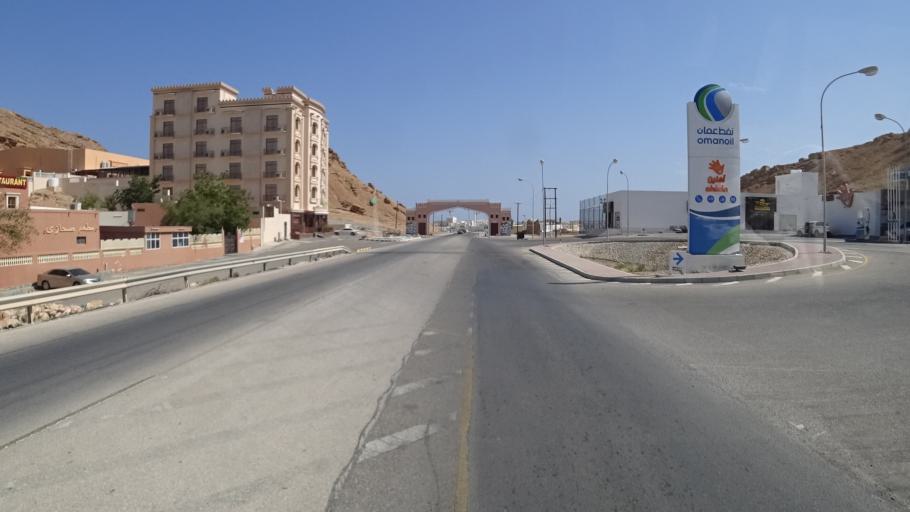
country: OM
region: Ash Sharqiyah
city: Sur
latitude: 22.5602
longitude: 59.5412
